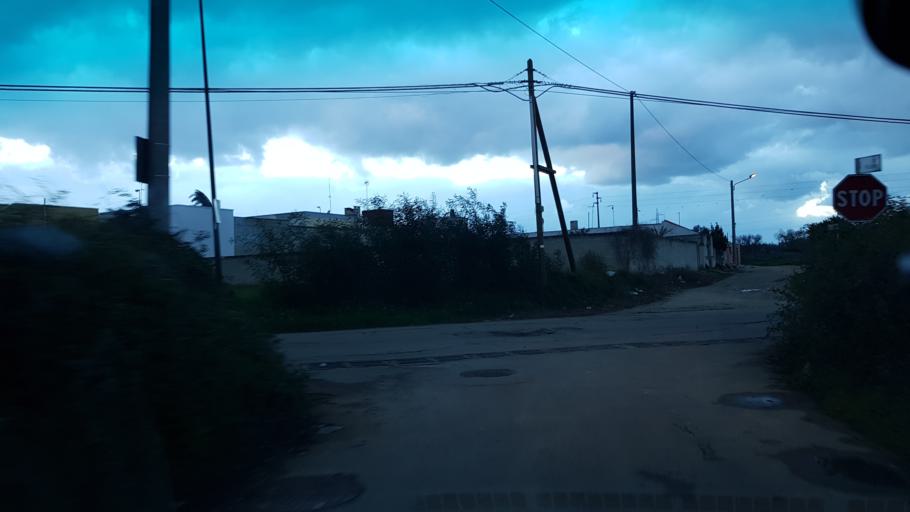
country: IT
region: Apulia
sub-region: Provincia di Brindisi
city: Torchiarolo
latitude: 40.4905
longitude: 18.0535
